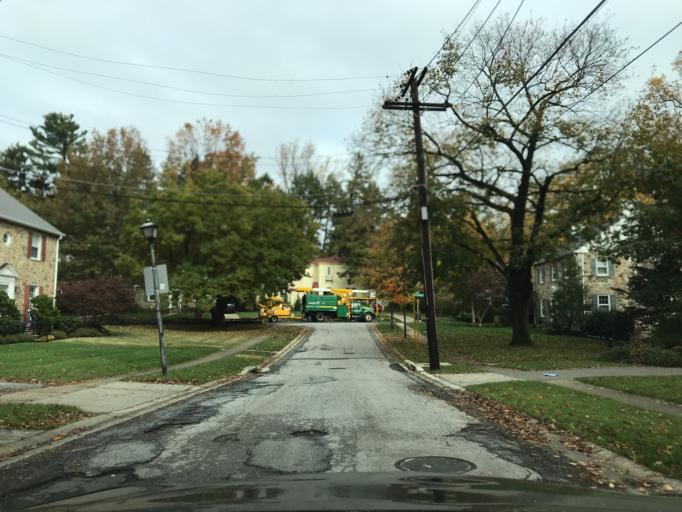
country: US
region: Maryland
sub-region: Baltimore County
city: Towson
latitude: 39.3822
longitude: -76.6029
